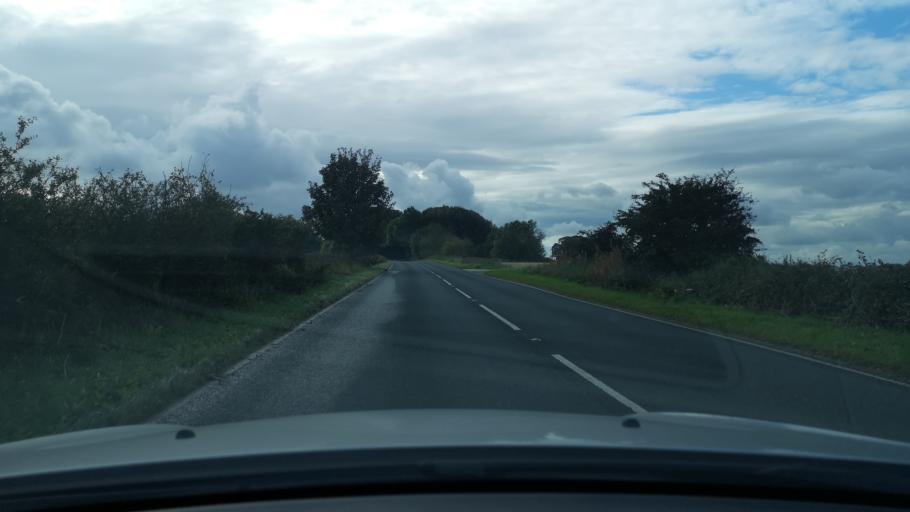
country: GB
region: England
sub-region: East Riding of Yorkshire
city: Walkington
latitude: 53.8058
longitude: -0.5470
